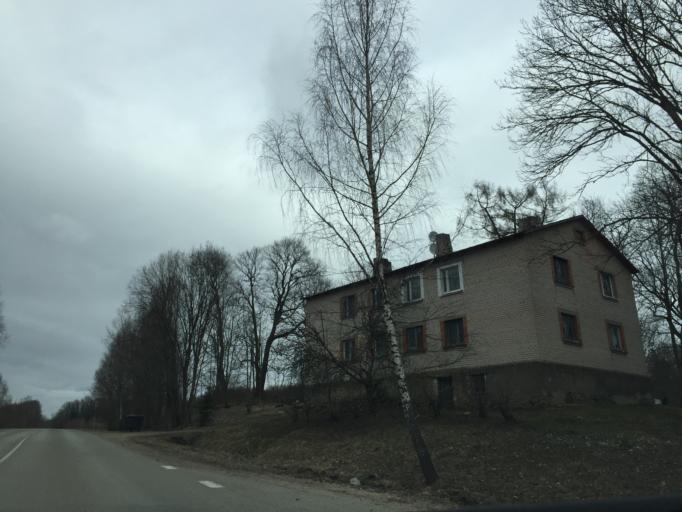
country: LV
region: Kraslavas Rajons
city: Kraslava
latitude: 55.9436
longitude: 27.1623
